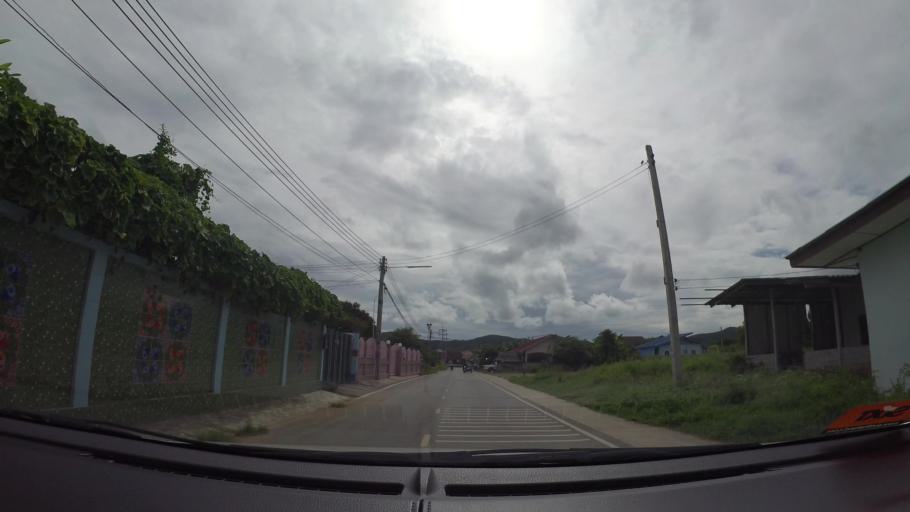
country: TH
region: Chon Buri
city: Sattahip
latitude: 12.7132
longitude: 100.8936
